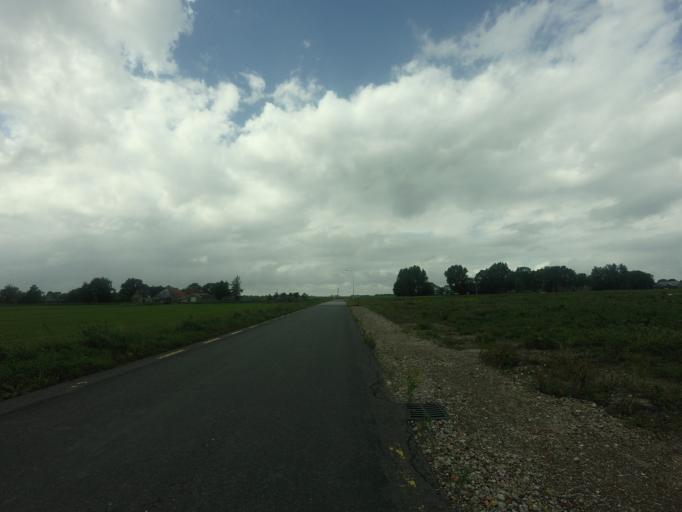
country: NL
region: Friesland
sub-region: Gemeente Skarsterlan
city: Joure
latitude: 52.9692
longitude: 5.7808
